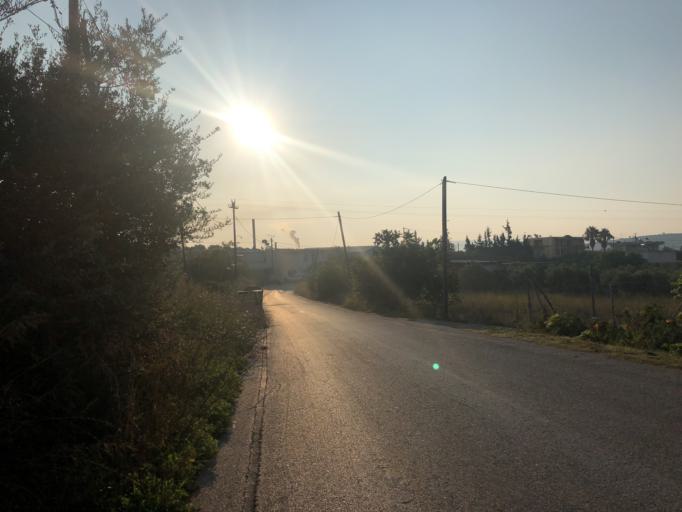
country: GR
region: Crete
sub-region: Nomos Chanias
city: Georgioupolis
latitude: 35.3478
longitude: 24.2864
